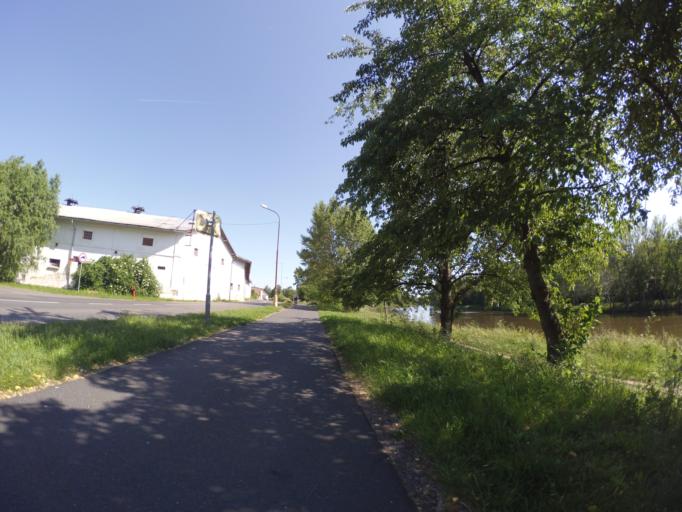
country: CZ
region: Central Bohemia
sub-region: Okres Nymburk
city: Podebrady
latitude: 50.1577
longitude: 15.1059
